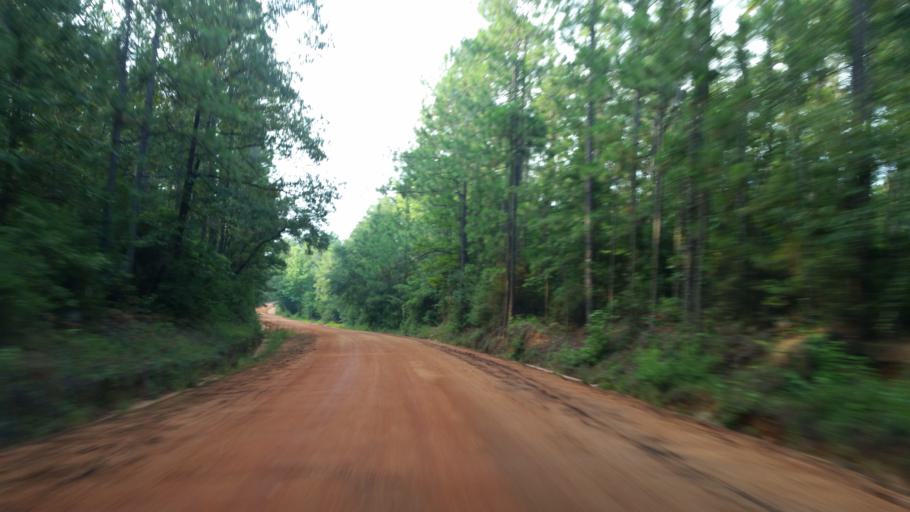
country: US
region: Alabama
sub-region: Escambia County
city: Atmore
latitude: 30.9579
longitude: -87.5730
